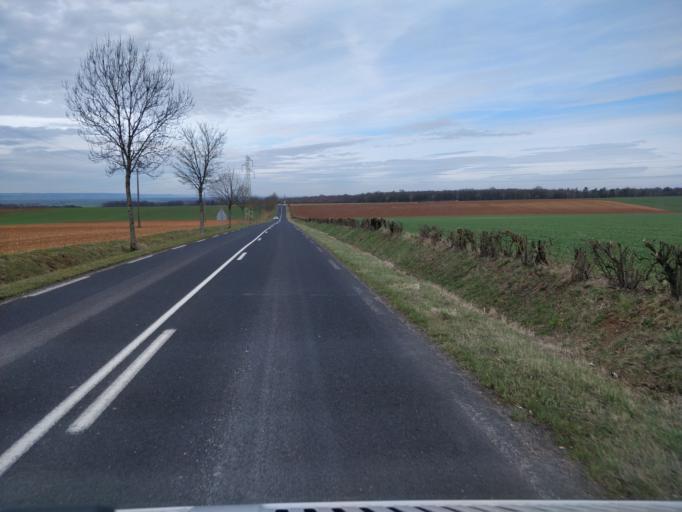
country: FR
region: Lorraine
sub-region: Departement de Meurthe-et-Moselle
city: Montauville
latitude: 48.9259
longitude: 5.9063
